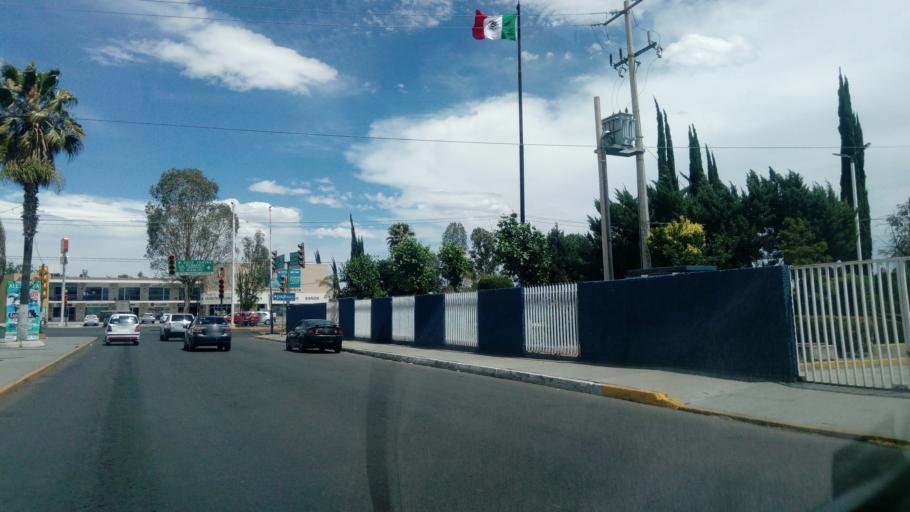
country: MX
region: Durango
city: Victoria de Durango
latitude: 23.9957
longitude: -104.6636
